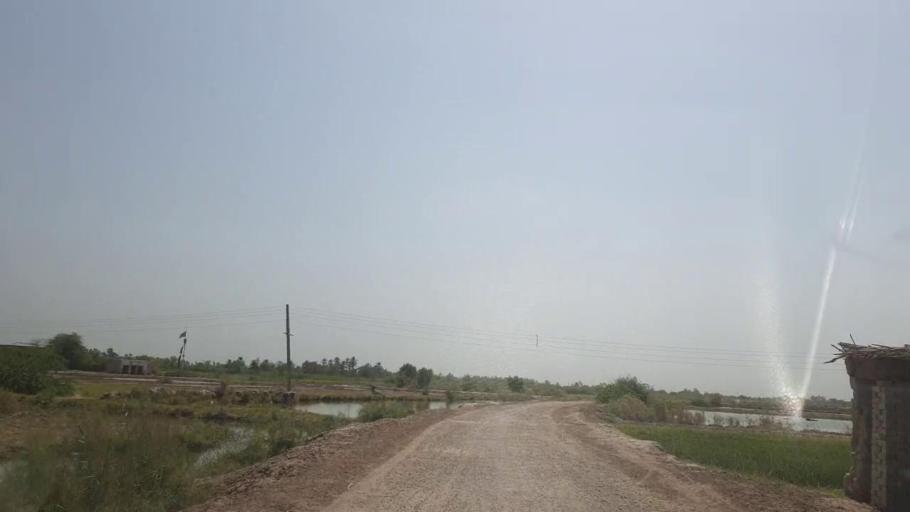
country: PK
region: Sindh
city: Gambat
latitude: 27.3152
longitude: 68.5398
